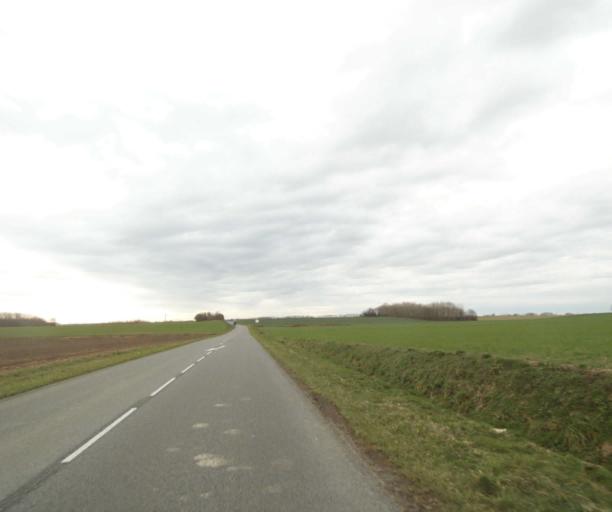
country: FR
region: Nord-Pas-de-Calais
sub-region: Departement du Nord
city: Sebourg
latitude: 50.3335
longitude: 3.6356
